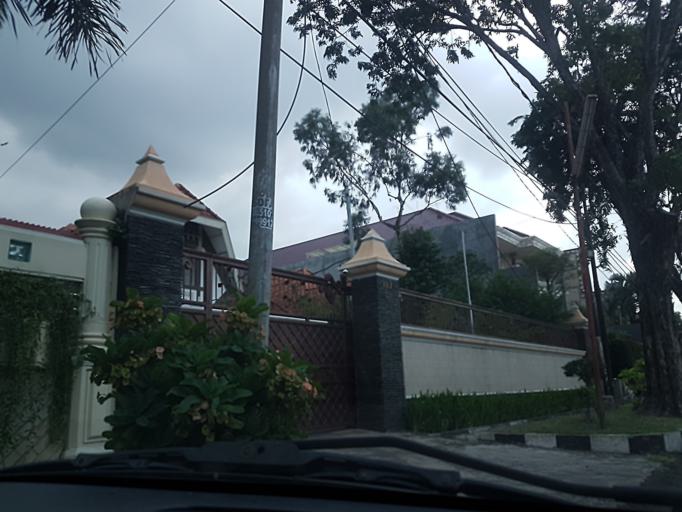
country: ID
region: East Java
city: Gubengairlangga
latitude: -7.2826
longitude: 112.7362
